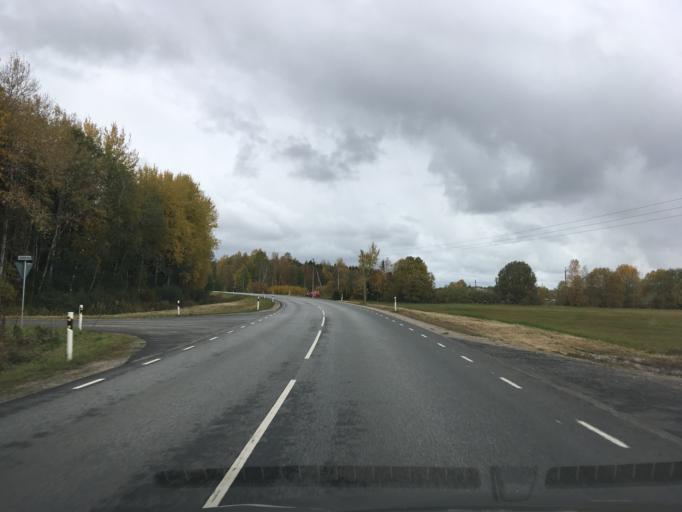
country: EE
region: Harju
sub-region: Anija vald
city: Kehra
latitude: 59.3198
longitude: 25.3427
